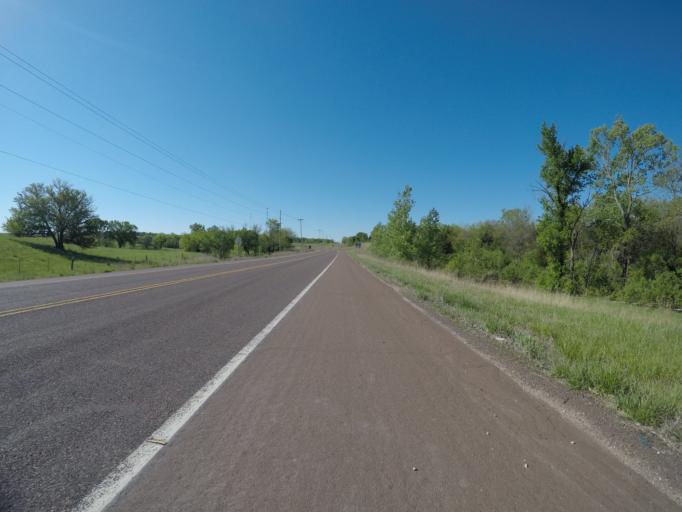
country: US
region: Kansas
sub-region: Douglas County
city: Lawrence
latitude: 39.0049
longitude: -95.3914
